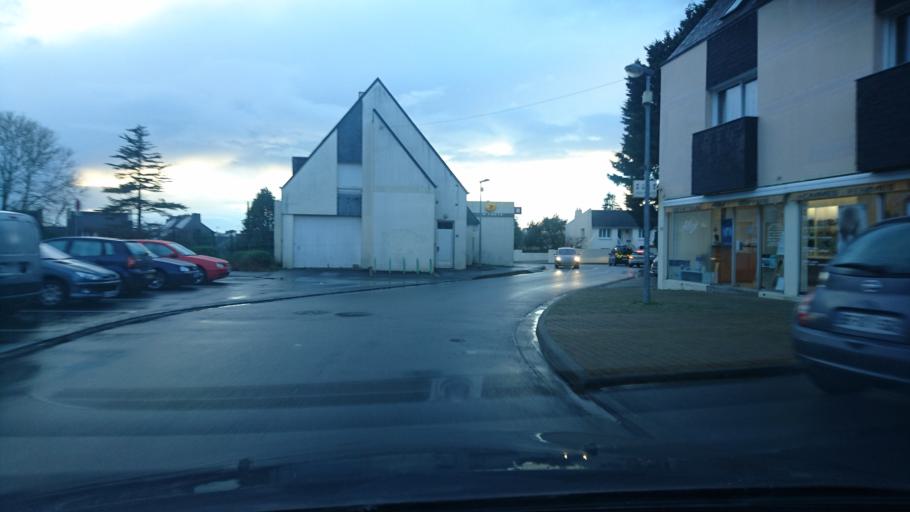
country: FR
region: Brittany
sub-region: Departement du Finistere
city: Guilers
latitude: 48.4243
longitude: -4.5596
